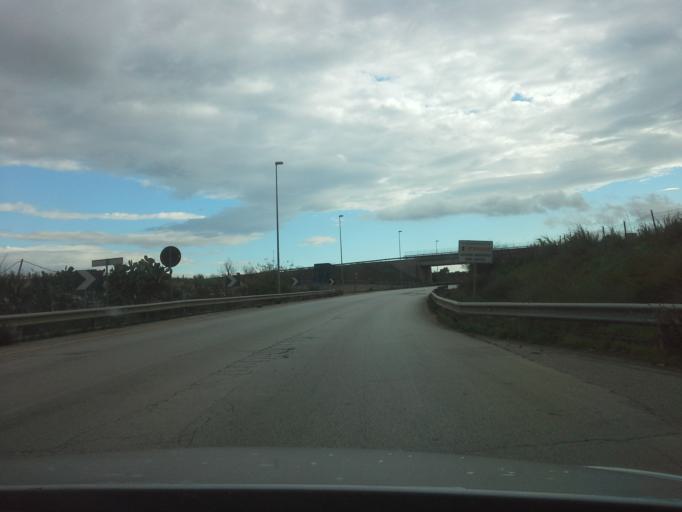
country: IT
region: Apulia
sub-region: Provincia di Bari
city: Turi
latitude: 40.9257
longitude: 16.9976
